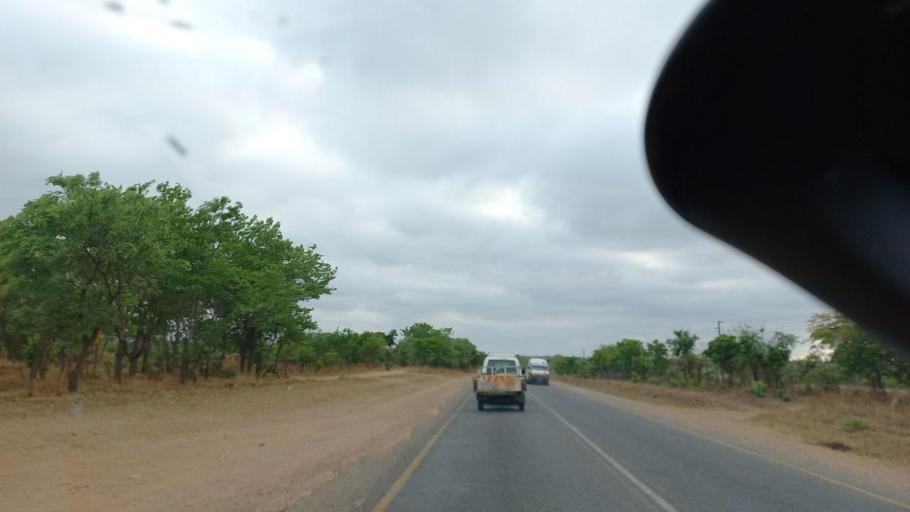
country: ZM
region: Lusaka
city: Chongwe
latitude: -15.2809
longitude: 28.7308
